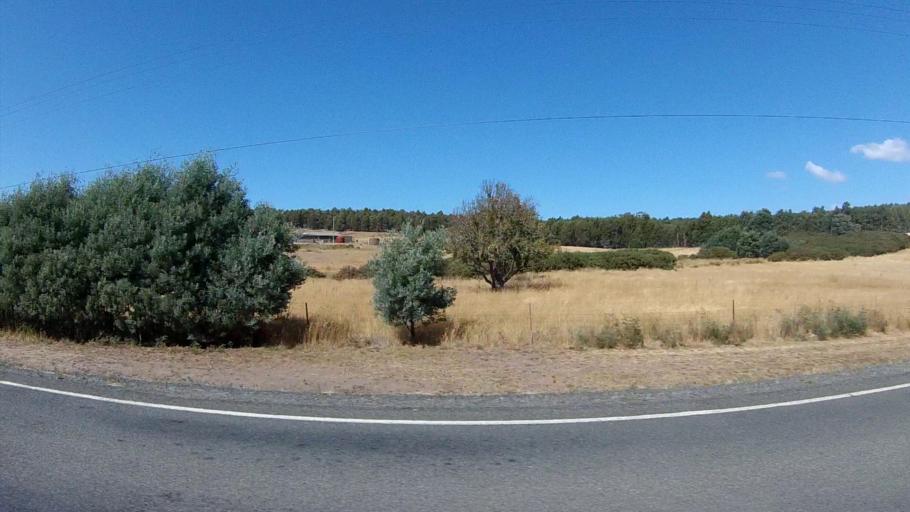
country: AU
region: Tasmania
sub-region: Sorell
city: Sorell
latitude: -42.6108
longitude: 147.7340
